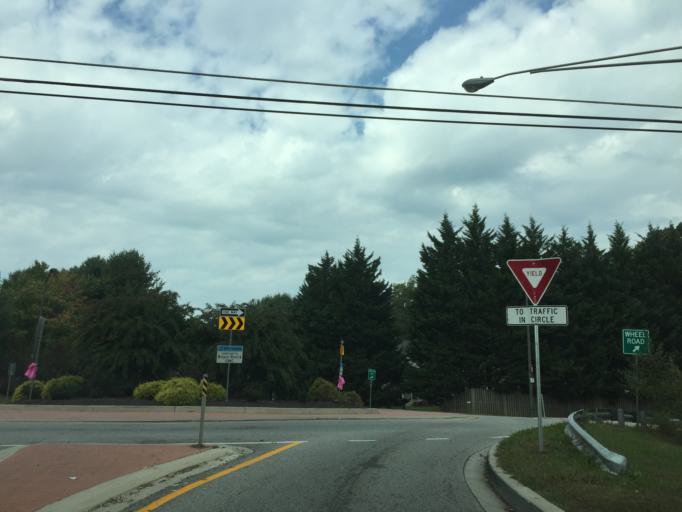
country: US
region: Maryland
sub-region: Harford County
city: Bel Air South
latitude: 39.4939
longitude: -76.3162
